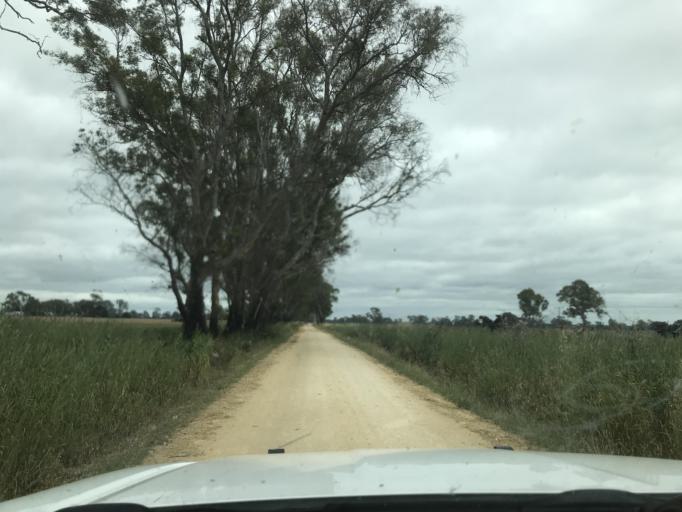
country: AU
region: South Australia
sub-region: Wattle Range
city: Penola
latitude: -37.1811
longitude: 141.0801
